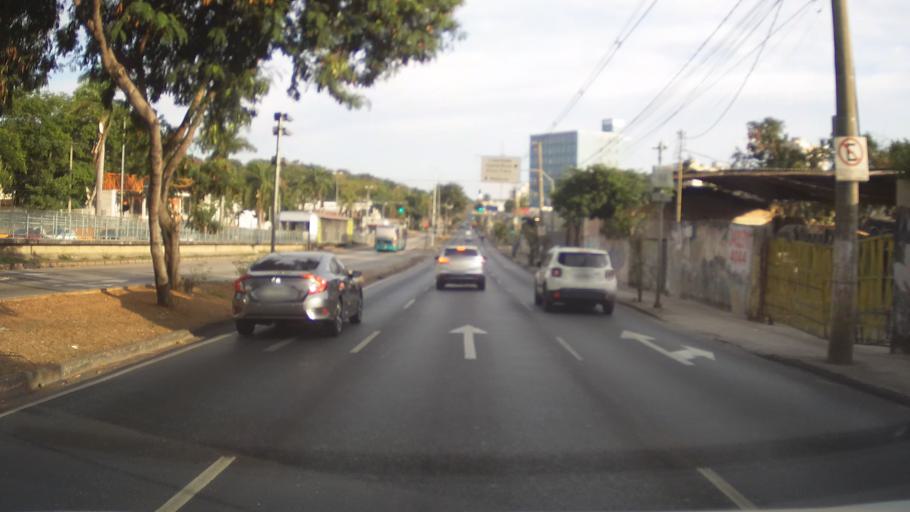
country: BR
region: Minas Gerais
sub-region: Belo Horizonte
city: Belo Horizonte
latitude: -19.8737
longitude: -43.9539
